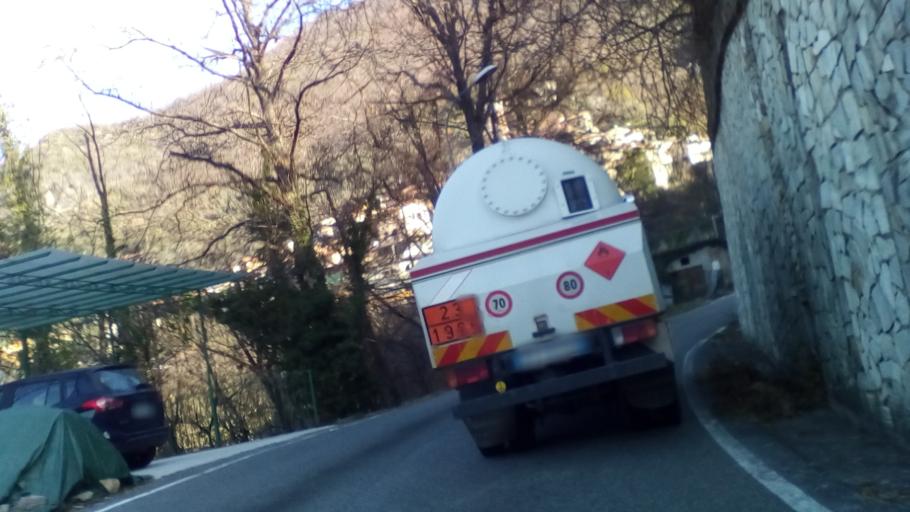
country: IT
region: Tuscany
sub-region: Provincia di Massa-Carrara
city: Montignoso
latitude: 44.0558
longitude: 10.1818
